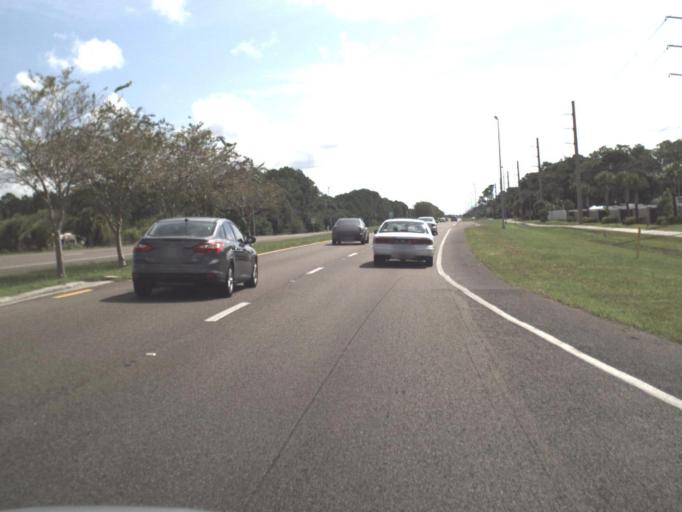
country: US
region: Florida
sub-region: Sarasota County
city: Warm Mineral Springs
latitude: 27.0484
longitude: -82.2845
